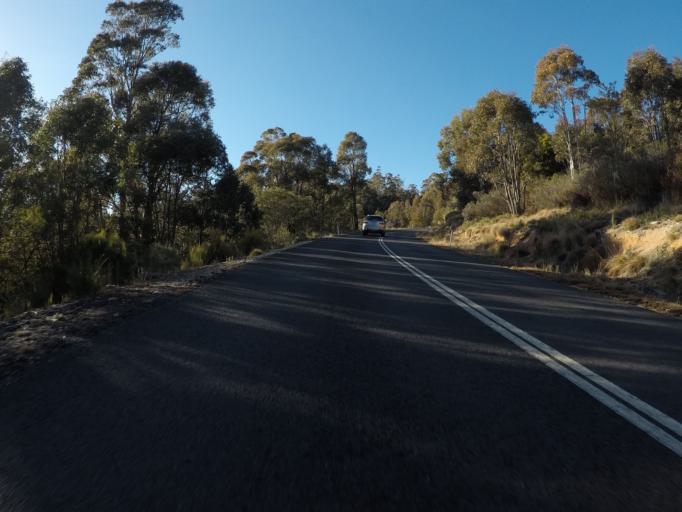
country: AU
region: Australian Capital Territory
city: Macarthur
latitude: -35.5025
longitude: 148.9215
